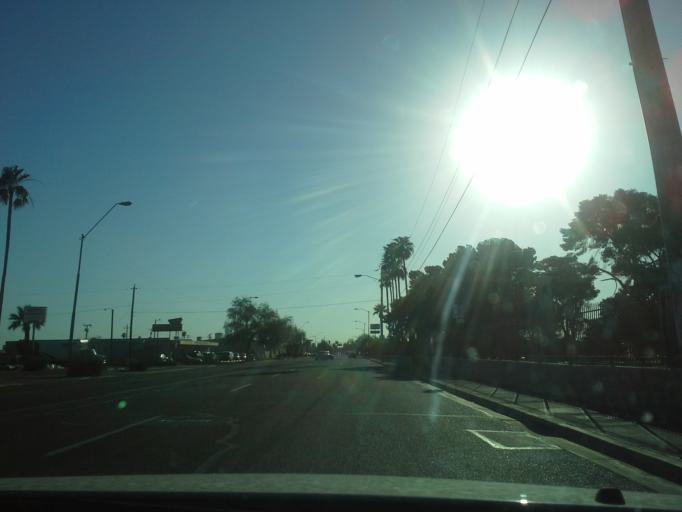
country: US
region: Arizona
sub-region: Maricopa County
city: Phoenix
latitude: 33.4513
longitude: -112.1099
